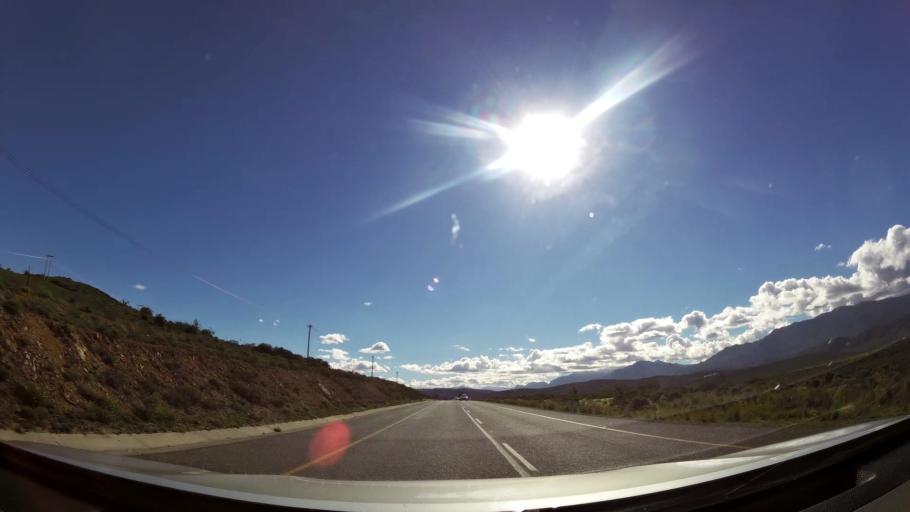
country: ZA
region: Western Cape
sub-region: Cape Winelands District Municipality
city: Worcester
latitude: -33.7598
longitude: 19.7363
